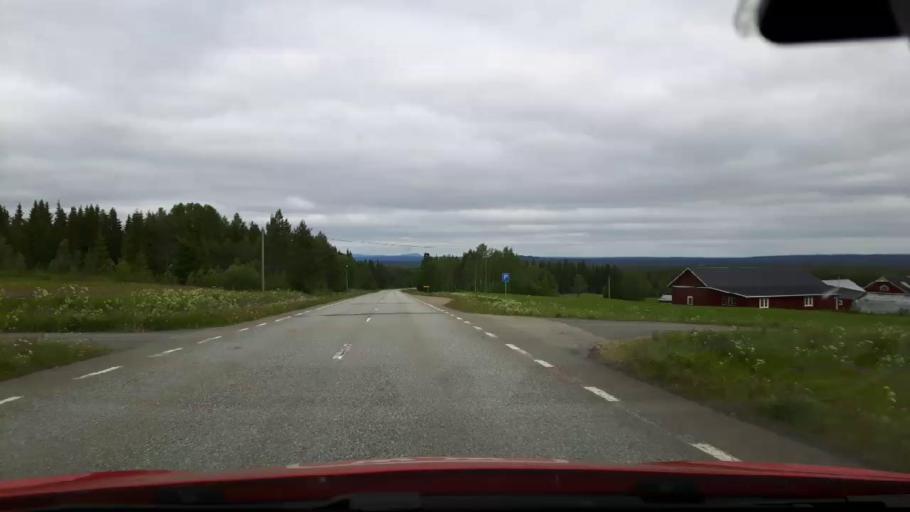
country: SE
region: Jaemtland
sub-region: Krokoms Kommun
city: Krokom
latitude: 63.5823
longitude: 14.6348
